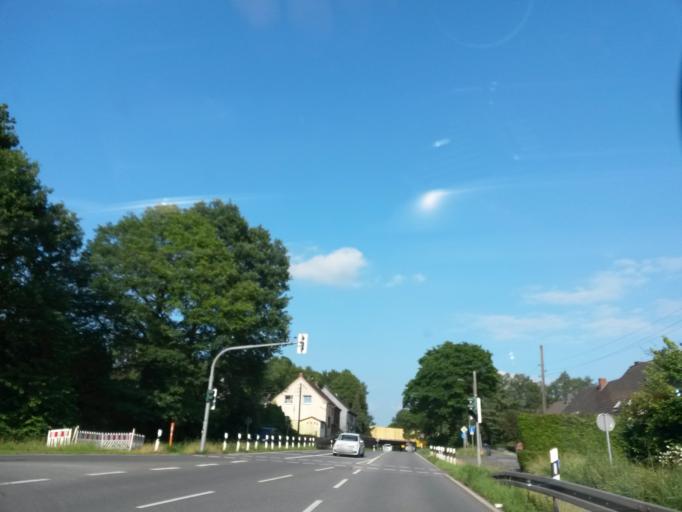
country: DE
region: North Rhine-Westphalia
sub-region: Regierungsbezirk Dusseldorf
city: Dinslaken
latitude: 51.5591
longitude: 6.8049
